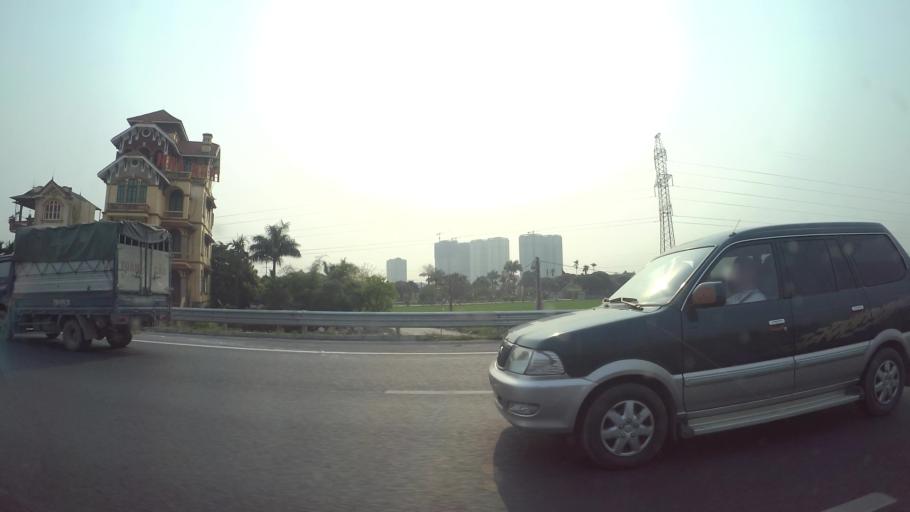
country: VN
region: Ha Noi
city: Van Dien
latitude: 20.9323
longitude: 105.8590
